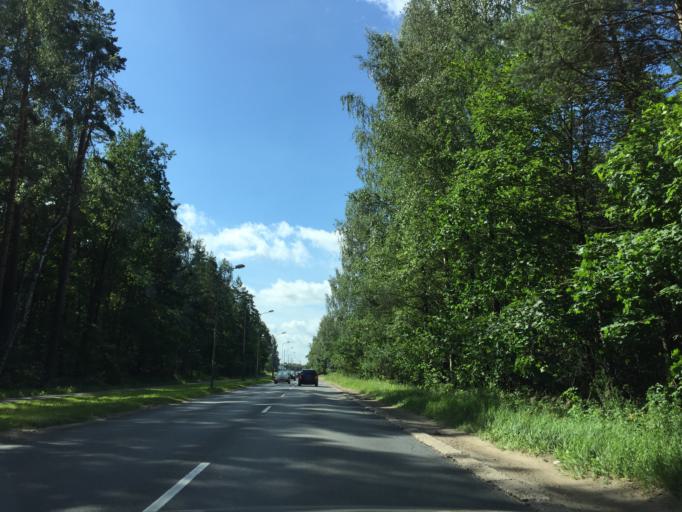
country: LV
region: Stopini
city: Ulbroka
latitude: 56.9637
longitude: 24.2527
